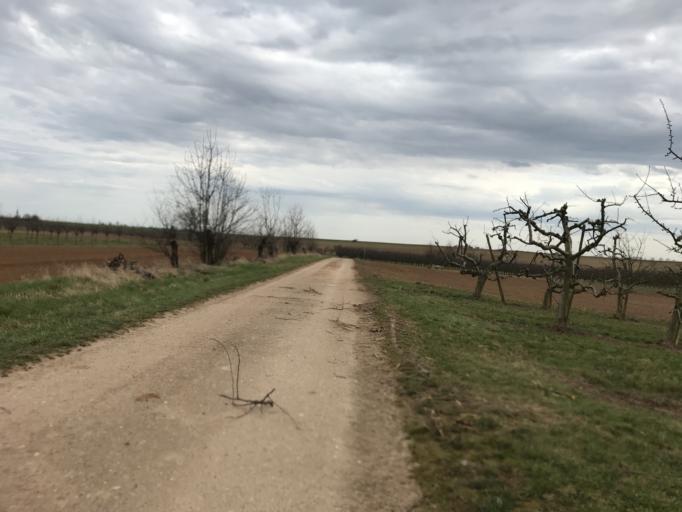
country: DE
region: Rheinland-Pfalz
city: Schwabenheim
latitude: 49.9524
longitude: 8.1017
